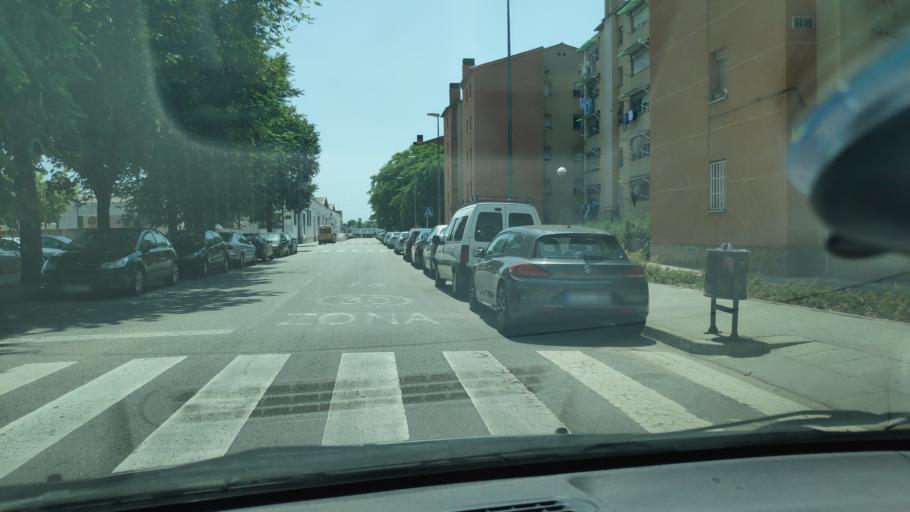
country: ES
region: Catalonia
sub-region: Provincia de Barcelona
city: Terrassa
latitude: 41.5599
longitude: 2.0360
